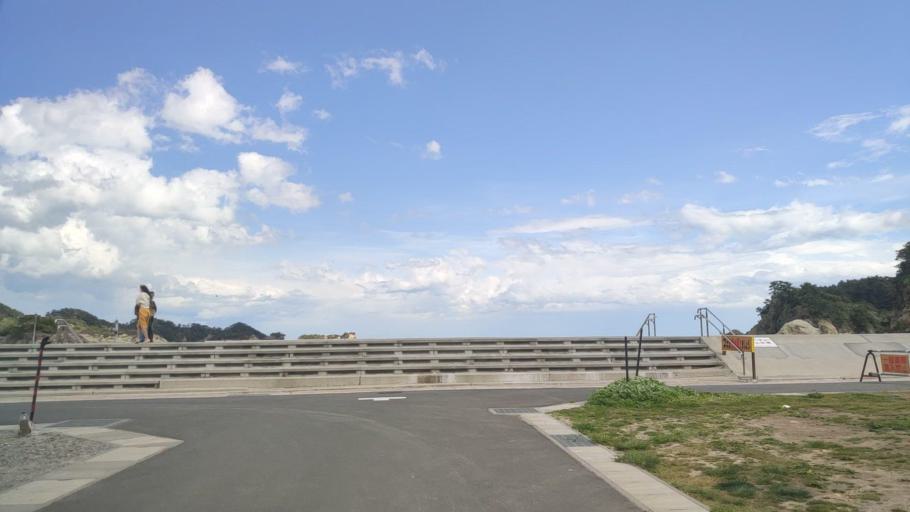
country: JP
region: Miyagi
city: Matsushima
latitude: 38.3246
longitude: 141.1551
